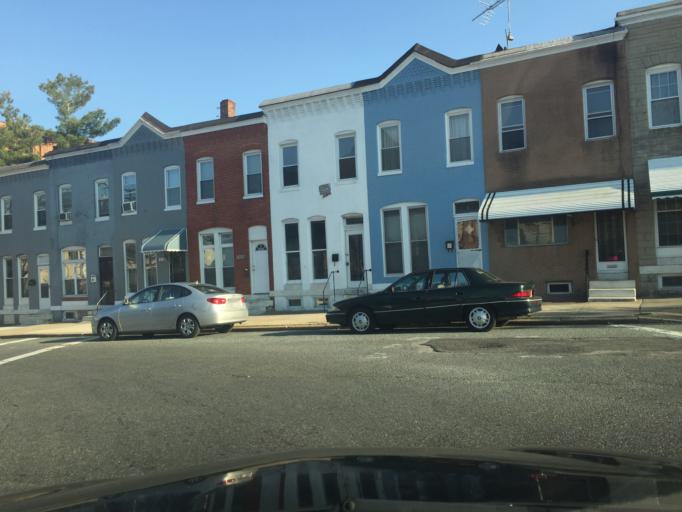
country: US
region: Maryland
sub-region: City of Baltimore
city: Baltimore
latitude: 39.3162
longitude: -76.6226
